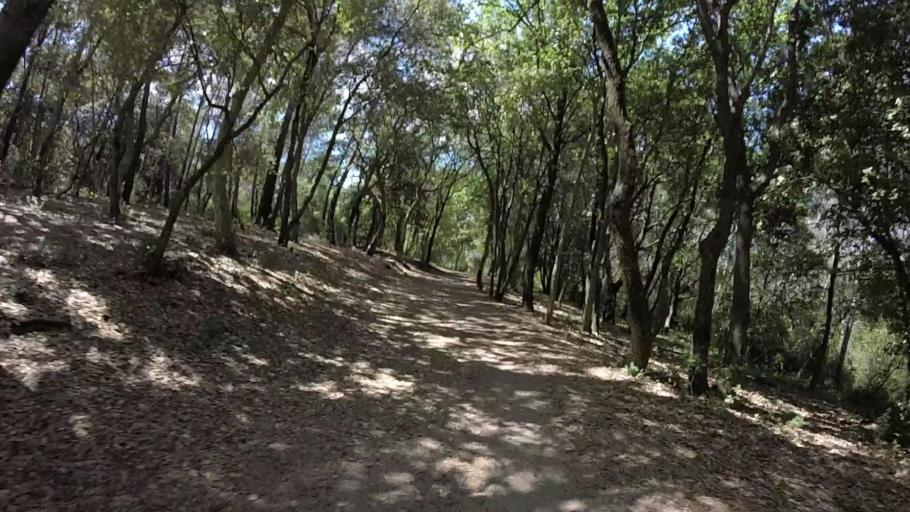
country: FR
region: Provence-Alpes-Cote d'Azur
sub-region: Departement des Alpes-Maritimes
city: Vallauris
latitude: 43.5976
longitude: 7.0412
